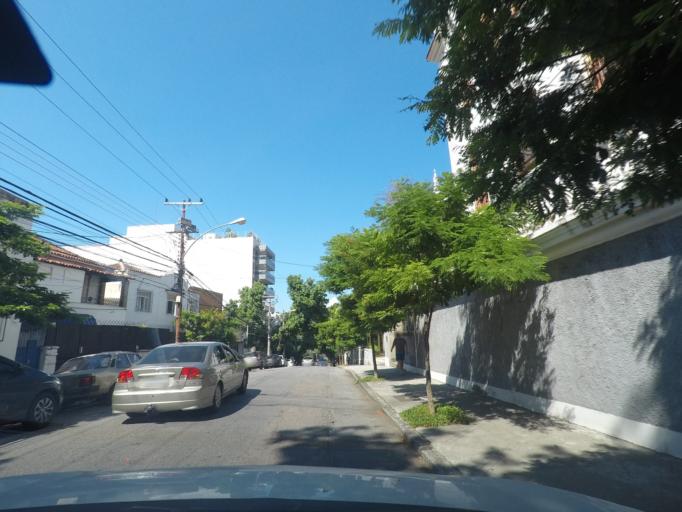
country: BR
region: Rio de Janeiro
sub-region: Rio De Janeiro
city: Rio de Janeiro
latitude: -22.9306
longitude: -43.2331
